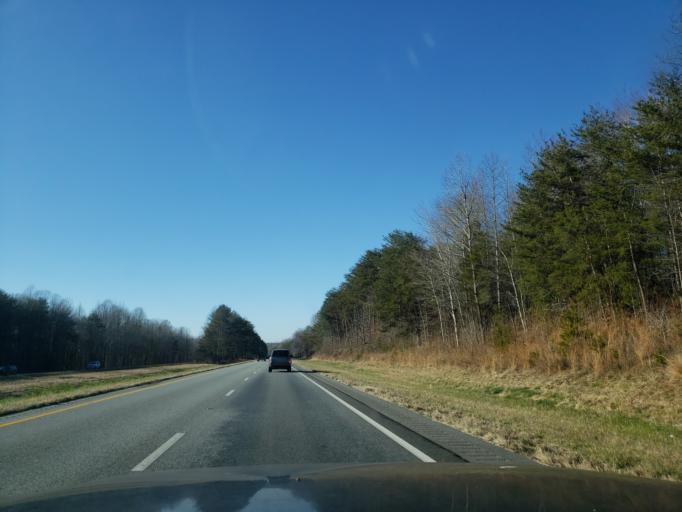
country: US
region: North Carolina
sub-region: Davidson County
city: Wallburg
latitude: 36.0318
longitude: -80.0743
